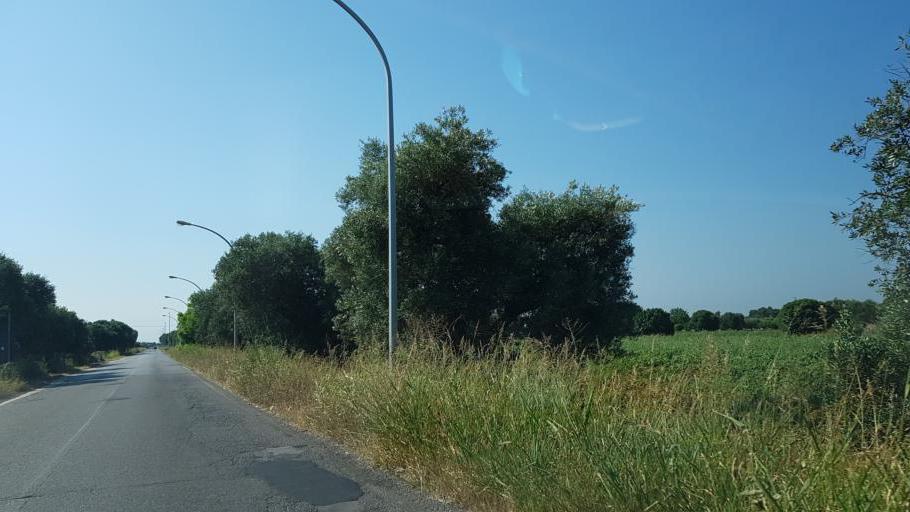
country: IT
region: Apulia
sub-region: Provincia di Brindisi
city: Mesagne
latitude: 40.5490
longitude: 17.8180
